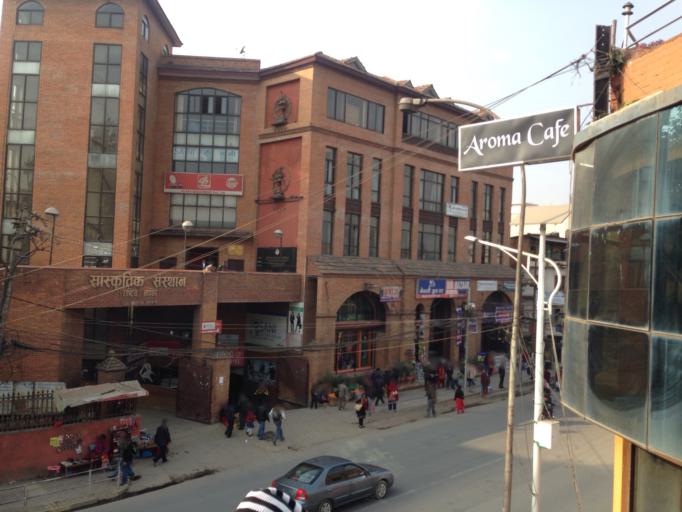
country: NP
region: Central Region
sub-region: Bagmati Zone
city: Kathmandu
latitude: 27.7088
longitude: 85.3146
